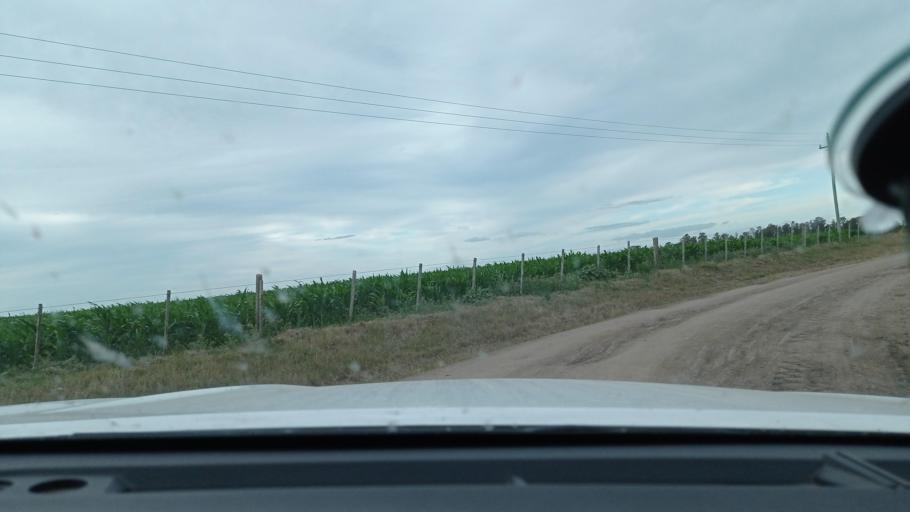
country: UY
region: Florida
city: Casupa
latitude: -34.1034
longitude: -55.7548
